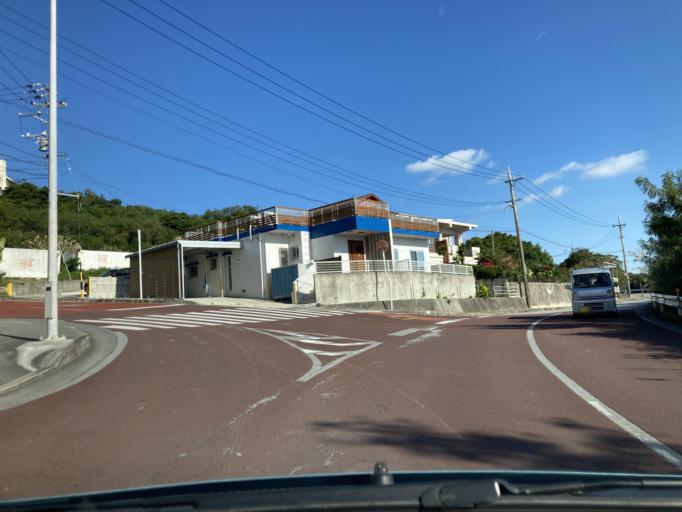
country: JP
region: Okinawa
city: Ginowan
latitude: 26.2215
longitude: 127.7371
